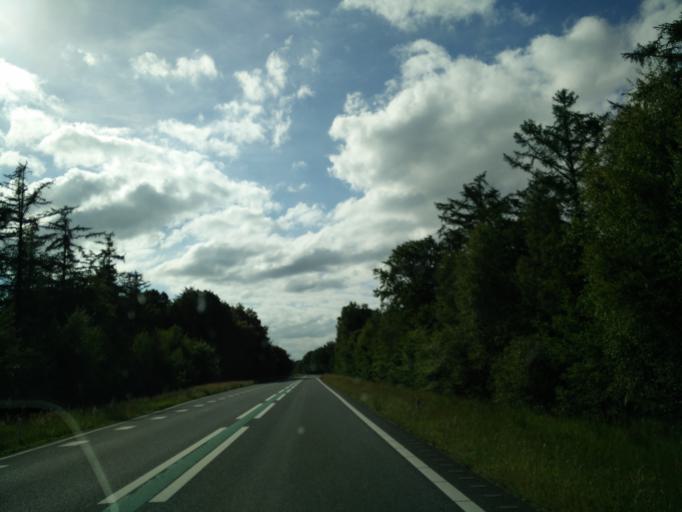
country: NL
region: Drenthe
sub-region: Gemeente Coevorden
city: Sleen
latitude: 52.8126
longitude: 6.6828
